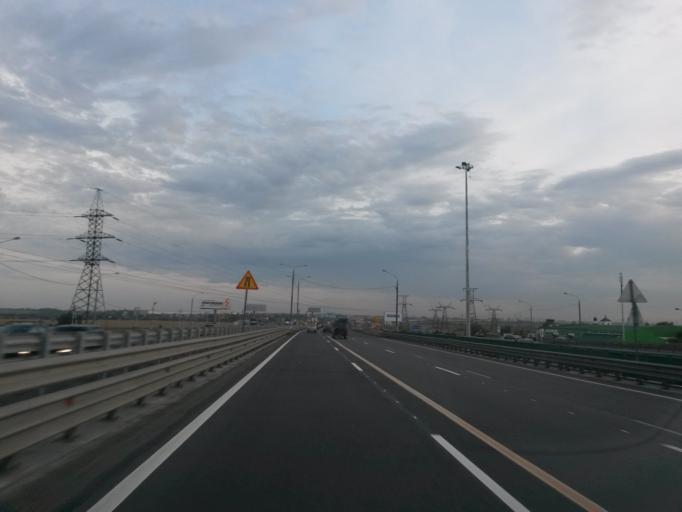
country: RU
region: Moskovskaya
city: Shcherbinka
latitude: 55.4651
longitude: 37.6186
